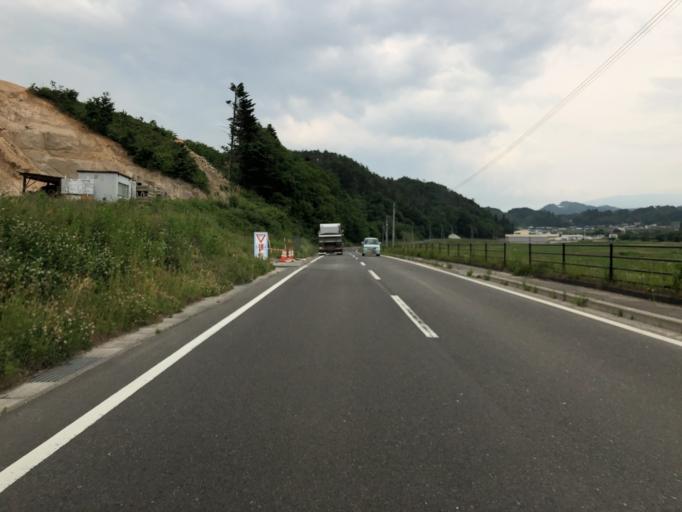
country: JP
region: Fukushima
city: Funehikimachi-funehiki
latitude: 37.4470
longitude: 140.6079
